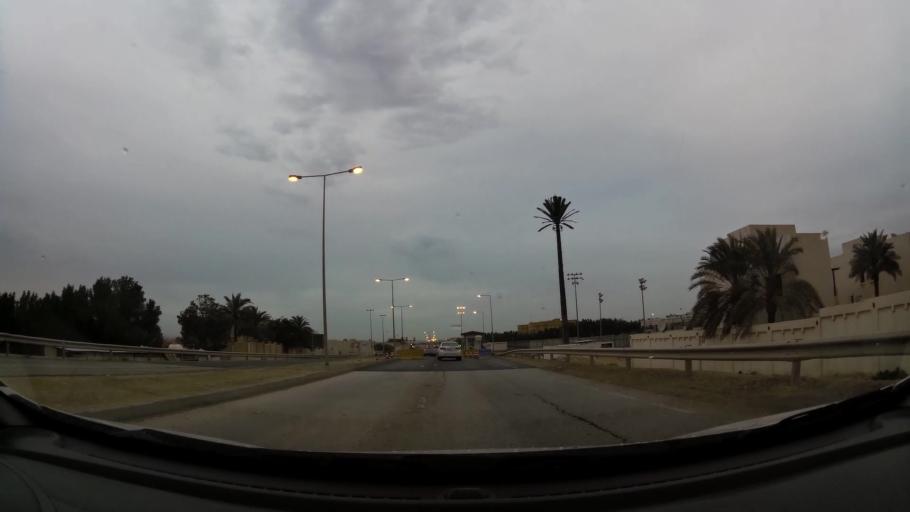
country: BH
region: Central Governorate
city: Madinat Hamad
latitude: 26.1399
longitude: 50.5171
